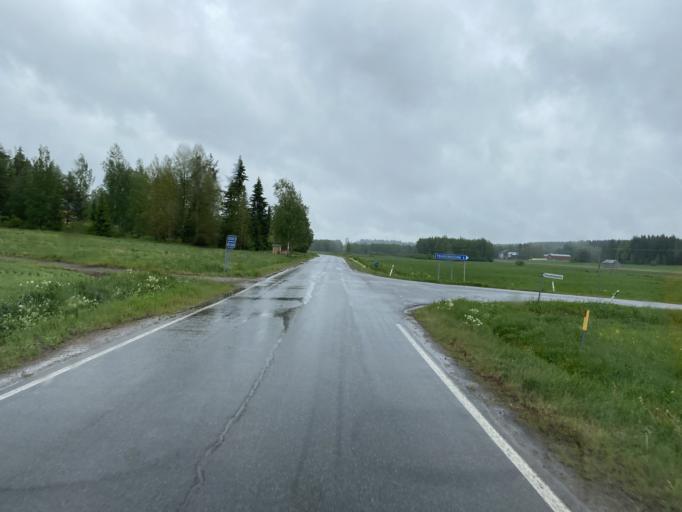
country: FI
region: Haeme
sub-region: Forssa
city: Humppila
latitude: 61.0424
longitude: 23.3941
